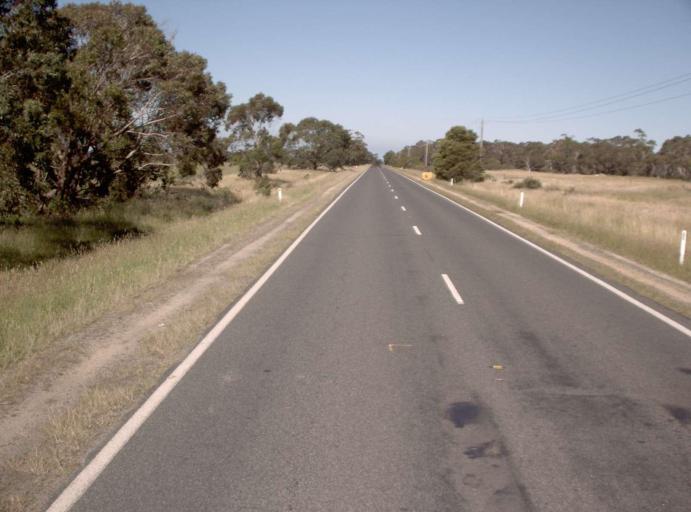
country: AU
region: Victoria
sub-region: Latrobe
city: Morwell
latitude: -38.6331
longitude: 146.5481
